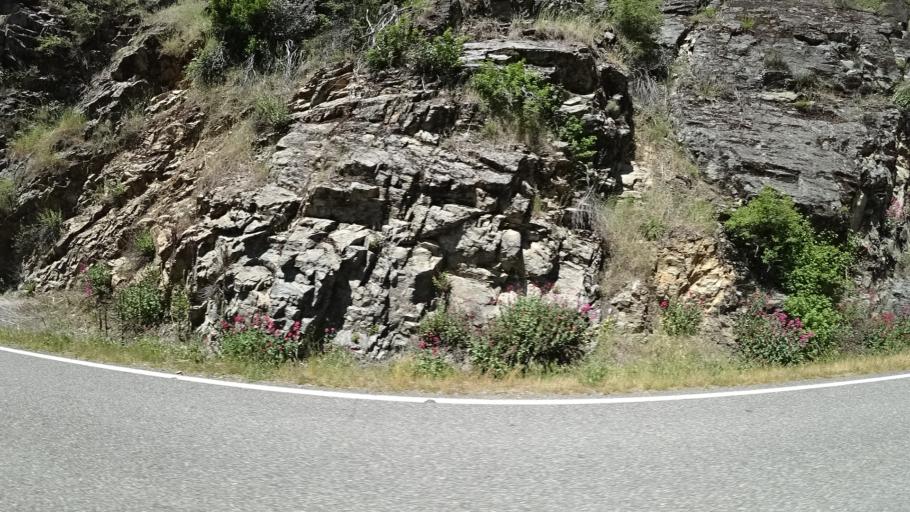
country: US
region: California
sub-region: Trinity County
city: Hayfork
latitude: 40.7519
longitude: -123.1642
